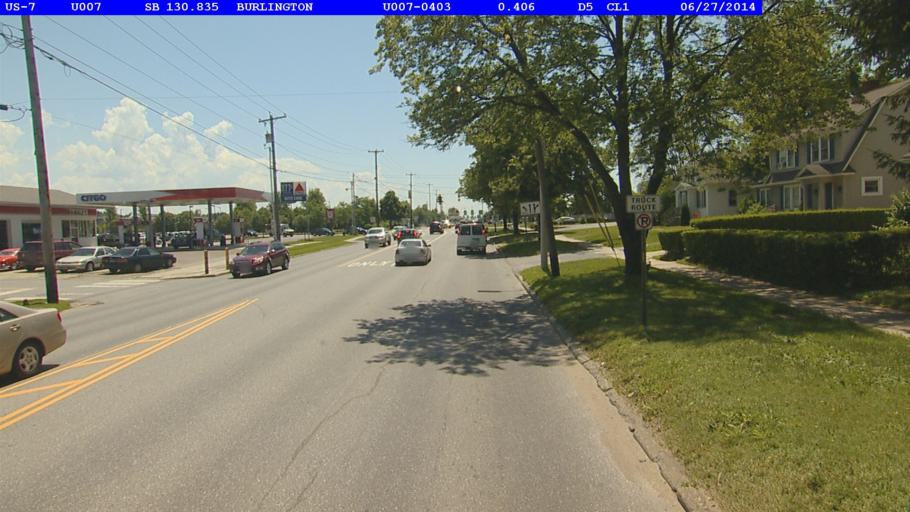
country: US
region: Vermont
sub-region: Chittenden County
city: Burlington
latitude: 44.4517
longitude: -73.2090
